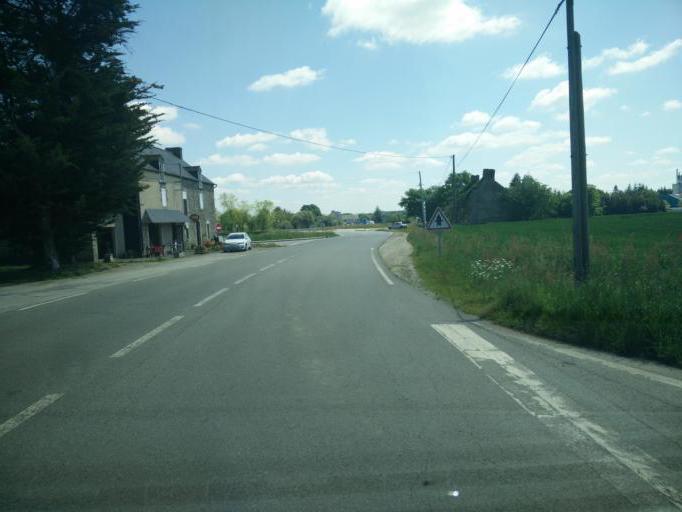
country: FR
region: Brittany
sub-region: Departement du Morbihan
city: Josselin
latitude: 47.9511
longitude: -2.5298
